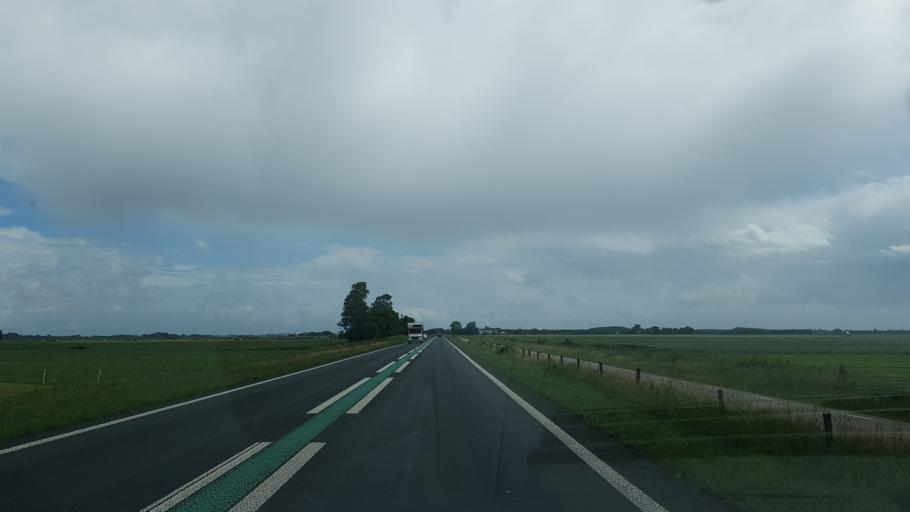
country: NL
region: Friesland
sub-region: Gemeente Ferwerderadiel
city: Burdaard
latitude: 53.2853
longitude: 5.9135
